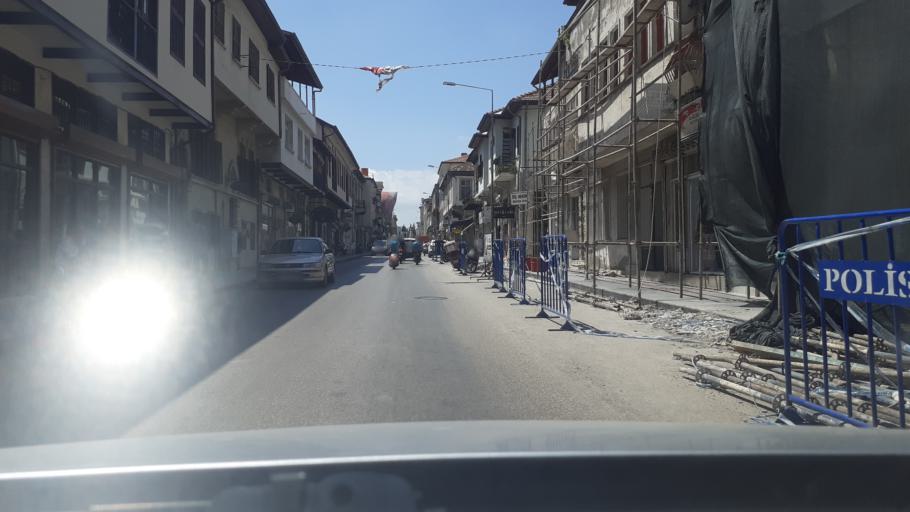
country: TR
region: Hatay
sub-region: Antakya Ilcesi
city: Antakya
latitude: 36.1993
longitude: 36.1635
